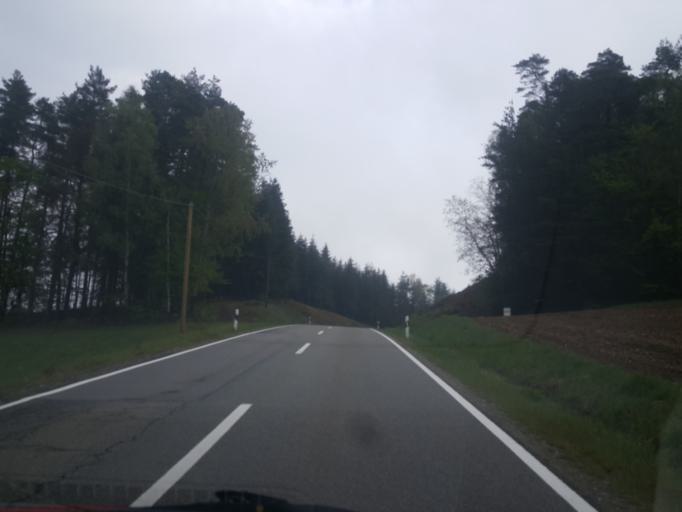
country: DE
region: Bavaria
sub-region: Lower Bavaria
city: Geiersthal
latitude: 49.0467
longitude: 12.9428
